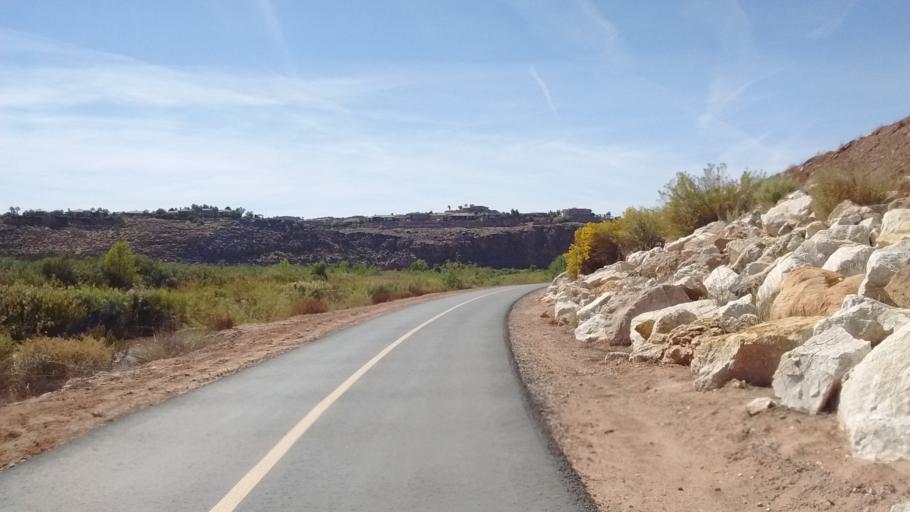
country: US
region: Utah
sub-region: Washington County
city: Saint George
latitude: 37.0894
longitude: -113.5382
